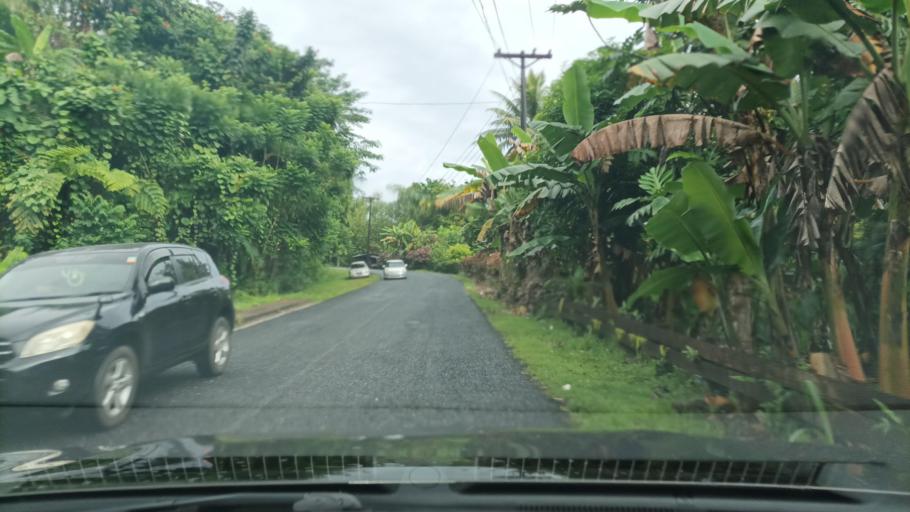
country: FM
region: Pohnpei
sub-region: Sokehs Municipality
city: Palikir - National Government Center
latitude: 6.9285
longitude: 158.1775
